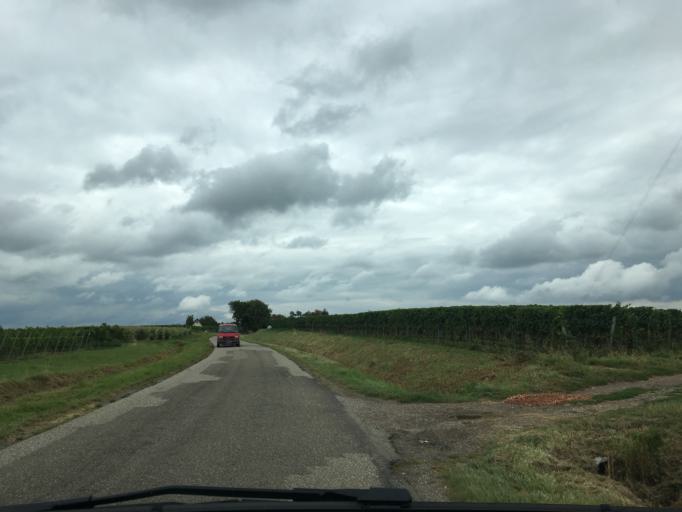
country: DE
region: Rheinland-Pfalz
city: Schweigen-Rechtenbach
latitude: 49.0383
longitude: 7.9626
